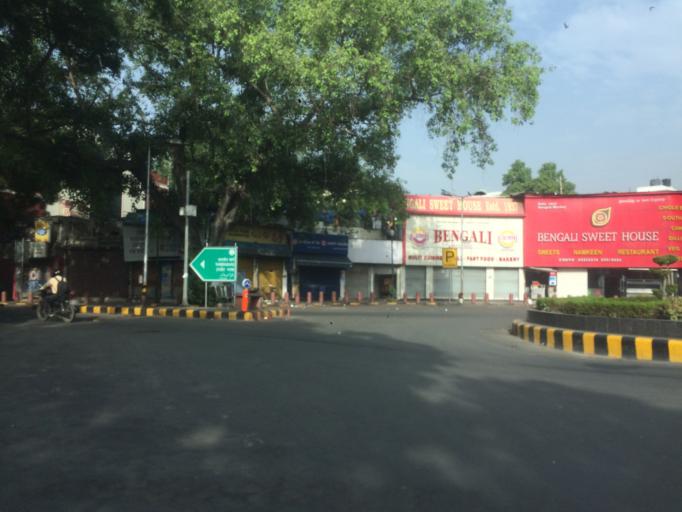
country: IN
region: NCT
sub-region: New Delhi
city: New Delhi
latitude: 28.6294
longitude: 77.2323
